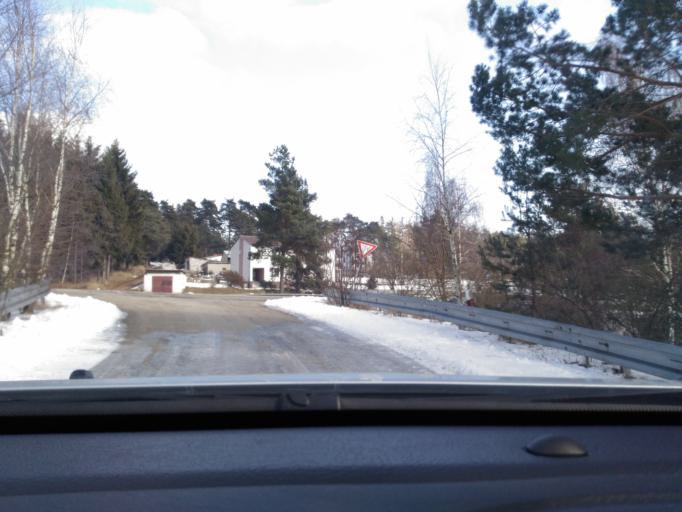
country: CZ
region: Vysocina
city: Krizanov
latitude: 49.4121
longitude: 16.0777
